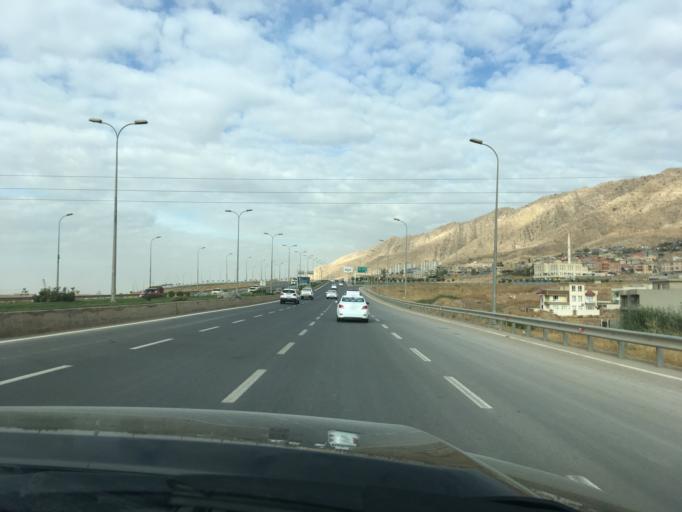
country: IQ
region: Dahuk
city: Sinah
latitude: 36.8485
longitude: 43.0559
